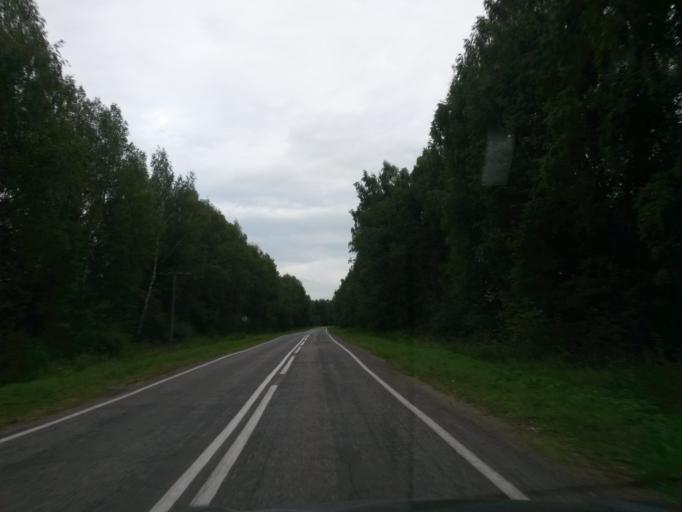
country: RU
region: Jaroslavl
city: Tutayev
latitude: 57.9246
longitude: 39.5084
